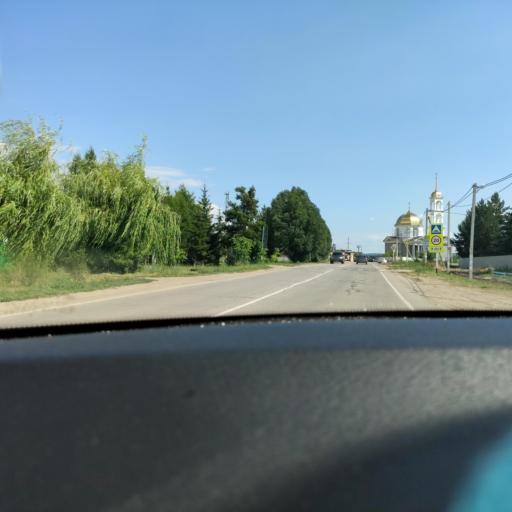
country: RU
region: Samara
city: Volzhskiy
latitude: 53.4494
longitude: 50.1760
